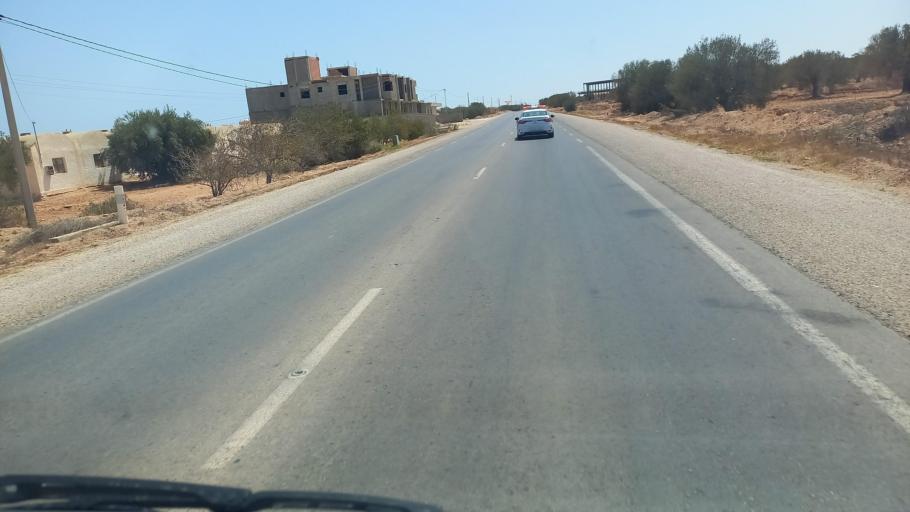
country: TN
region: Madanin
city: Zarzis
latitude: 33.5500
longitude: 11.0672
